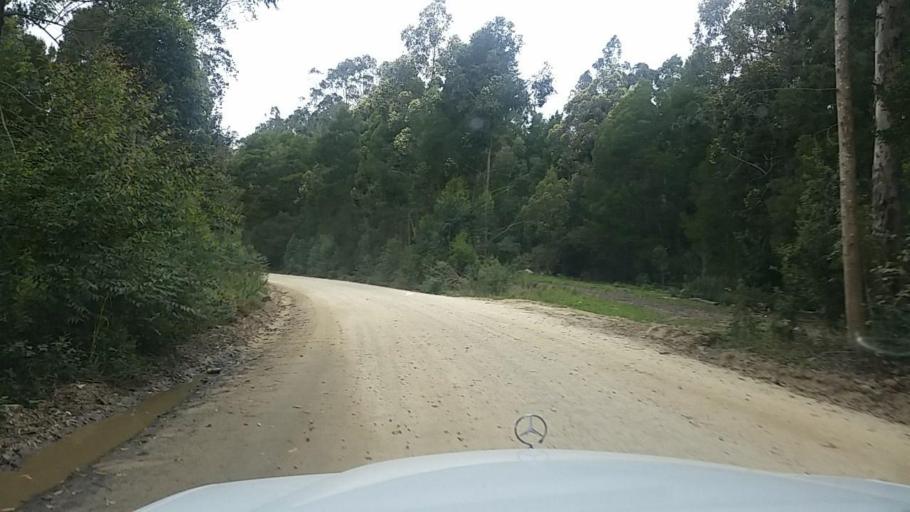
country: ZA
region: Western Cape
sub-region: Eden District Municipality
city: Knysna
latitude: -33.9802
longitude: 23.1368
